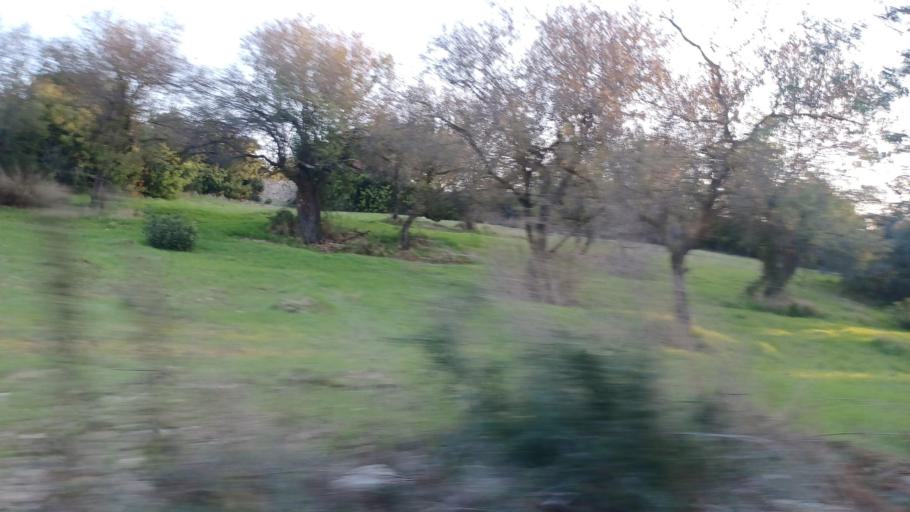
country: CY
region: Pafos
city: Tala
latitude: 34.9380
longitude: 32.5073
